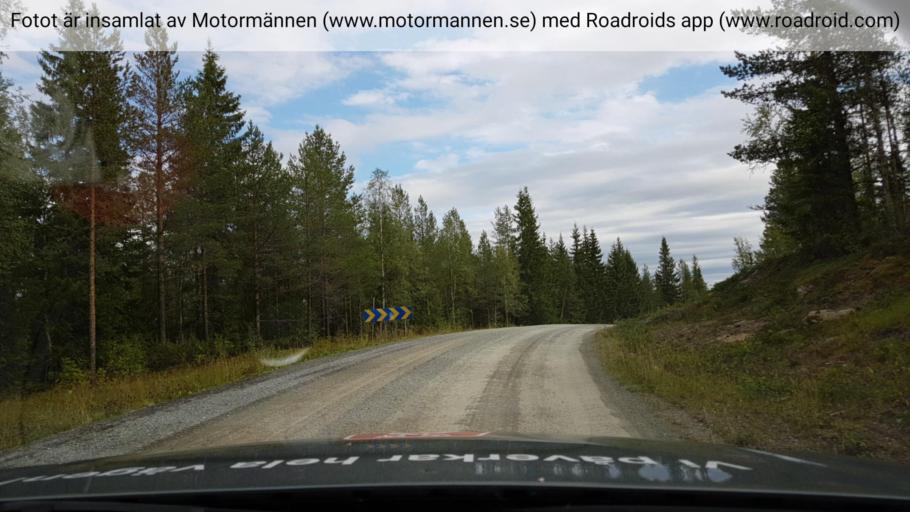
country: SE
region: Jaemtland
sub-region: Krokoms Kommun
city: Valla
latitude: 63.6640
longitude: 13.7300
